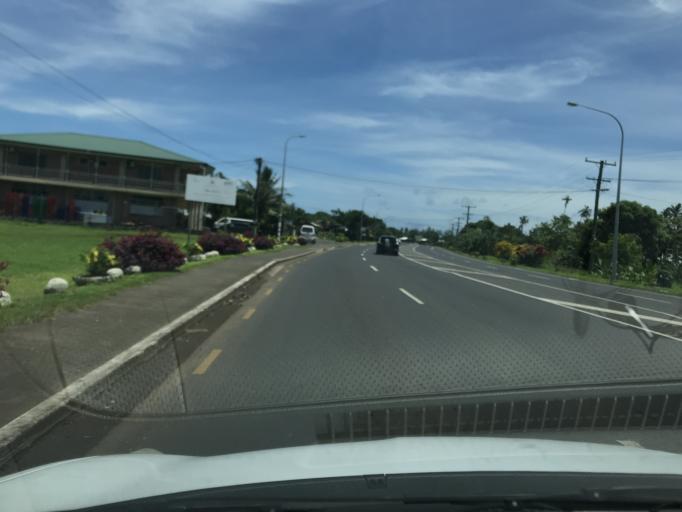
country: WS
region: Tuamasaga
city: Vaiusu
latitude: -13.8313
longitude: -171.7916
